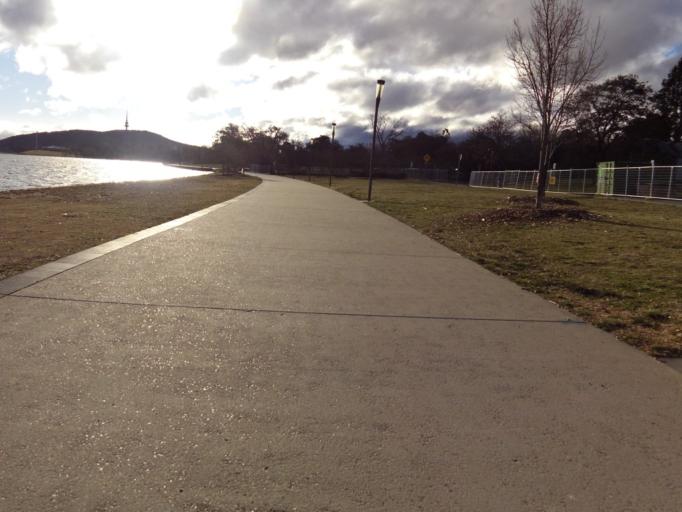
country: AU
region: Australian Capital Territory
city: Canberra
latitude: -35.2935
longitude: 149.1418
